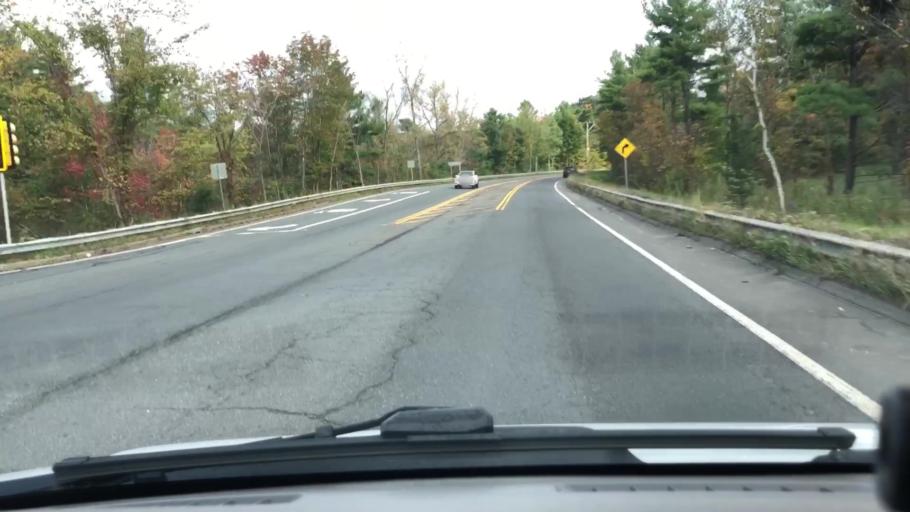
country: US
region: Massachusetts
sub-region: Berkshire County
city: Lanesborough
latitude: 42.4888
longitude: -73.2028
